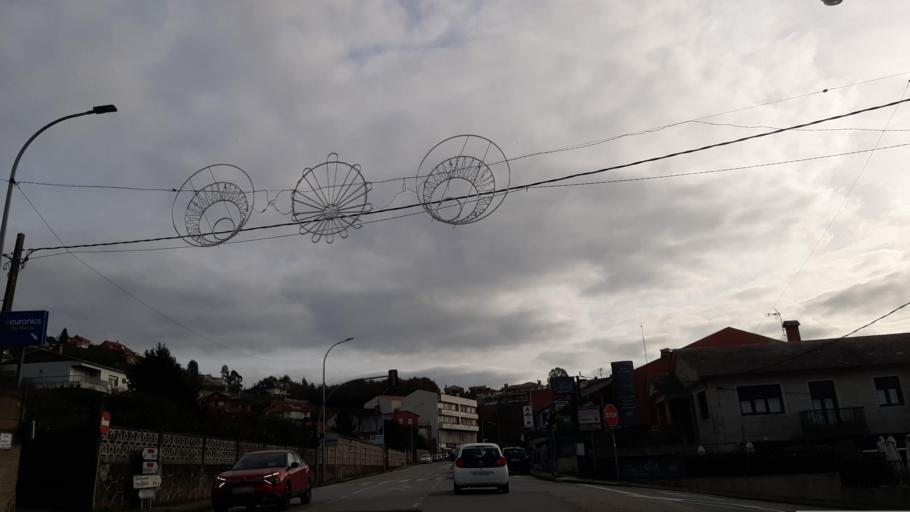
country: ES
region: Galicia
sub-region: Provincia de Pontevedra
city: Nigran
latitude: 42.1617
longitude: -8.8012
